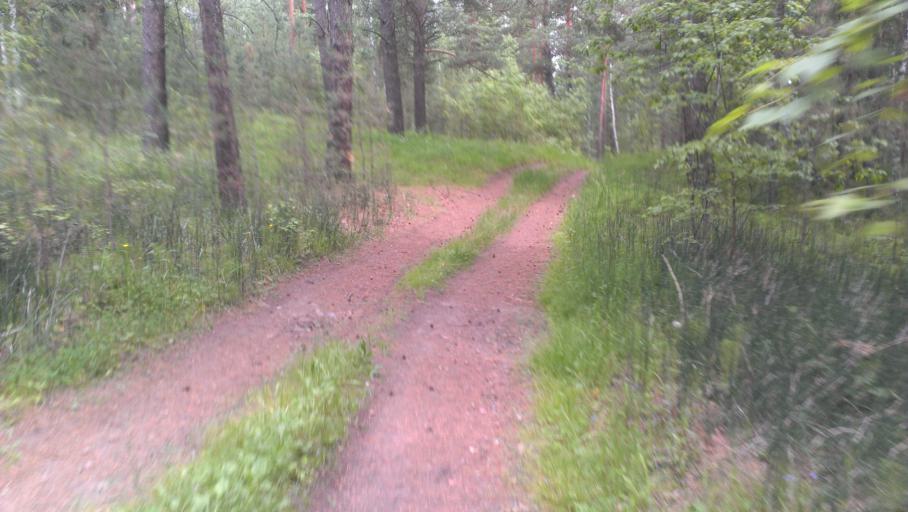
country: RU
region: Altai Krai
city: Sannikovo
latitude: 53.3494
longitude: 84.0371
